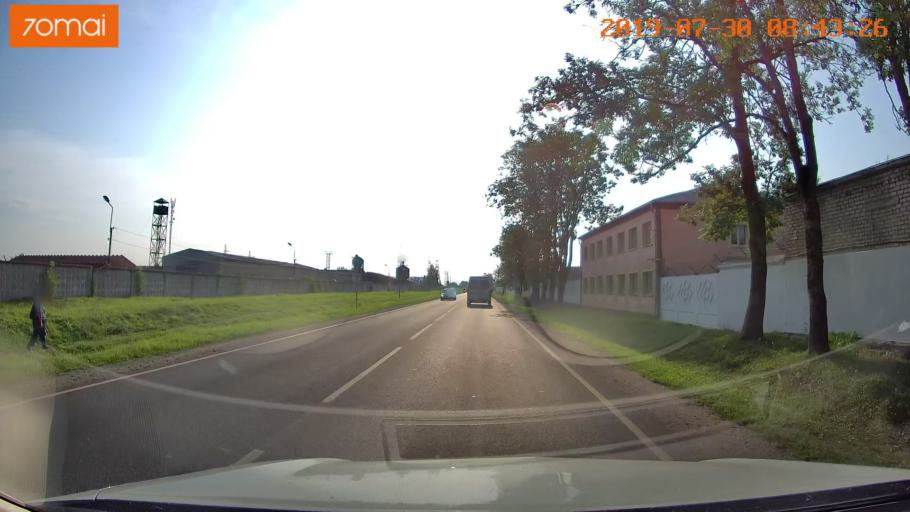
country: RU
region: Kaliningrad
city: Chernyakhovsk
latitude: 54.6270
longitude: 21.8409
